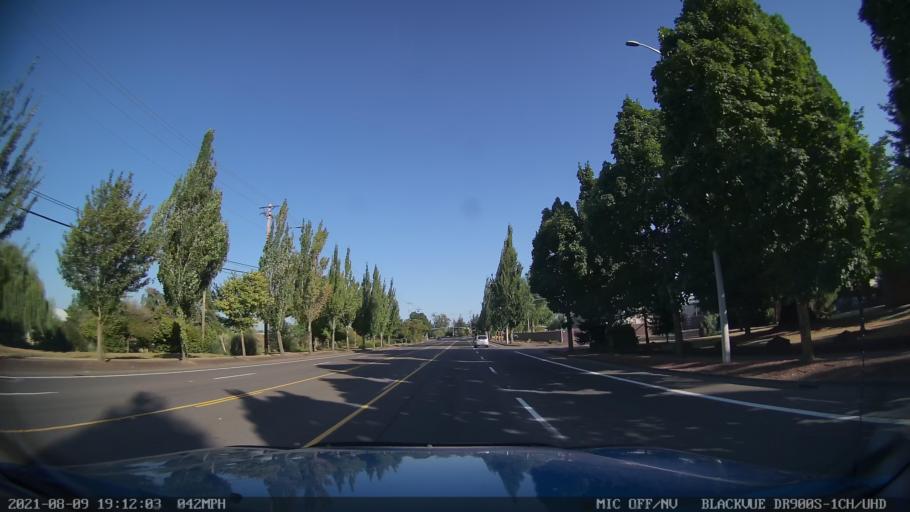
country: US
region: Oregon
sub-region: Marion County
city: Four Corners
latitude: 44.9306
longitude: -123.0062
